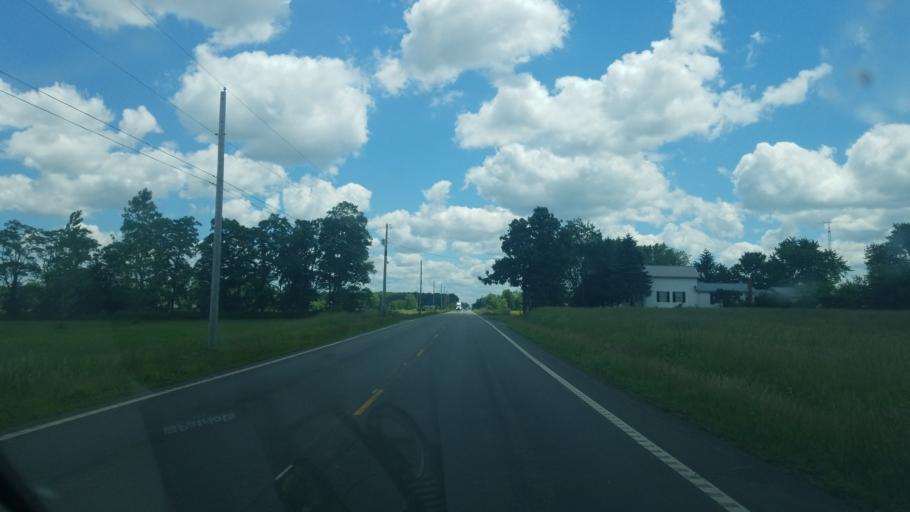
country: US
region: Ohio
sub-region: Huron County
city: New London
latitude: 41.0295
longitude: -82.3417
